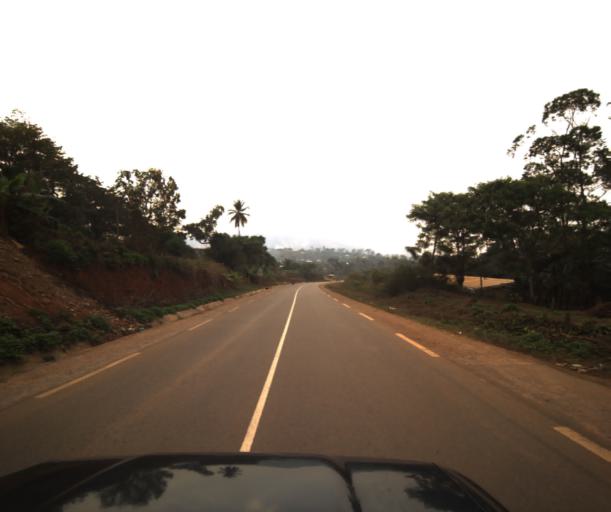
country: CM
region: Centre
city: Mbankomo
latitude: 3.7932
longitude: 11.4499
